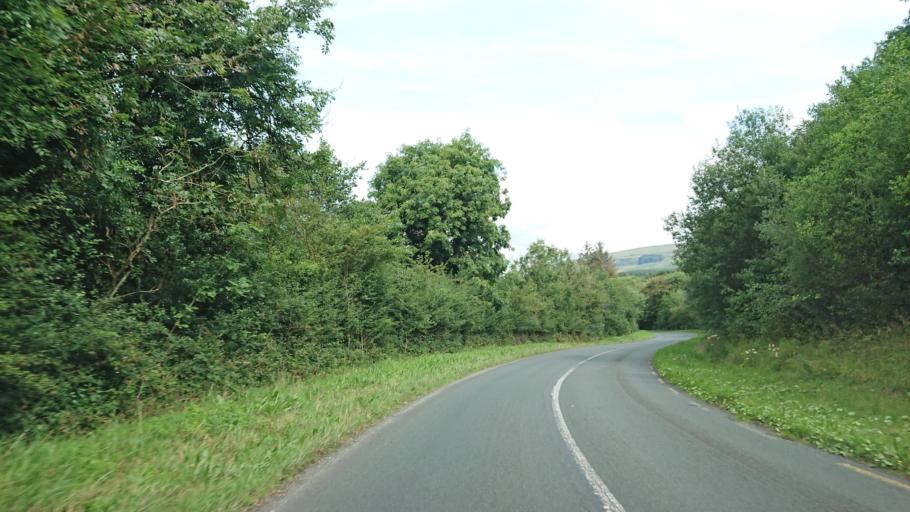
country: IE
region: Connaught
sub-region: County Leitrim
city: Carrick-on-Shannon
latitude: 54.0651
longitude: -8.0369
